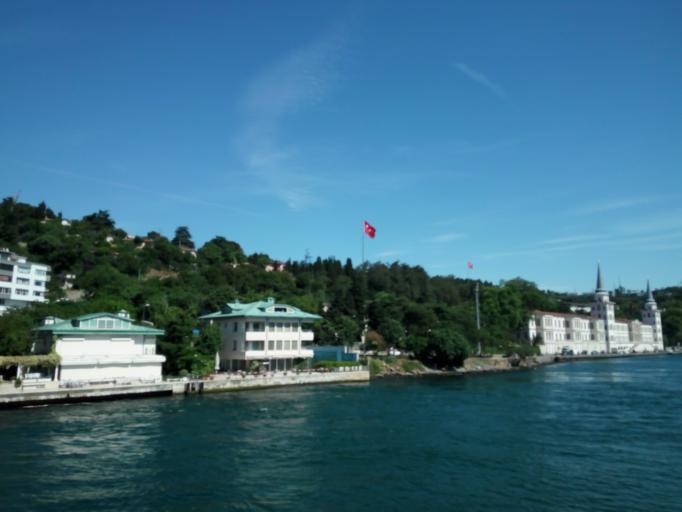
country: TR
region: Istanbul
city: UEskuedar
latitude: 41.0616
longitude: 29.0515
